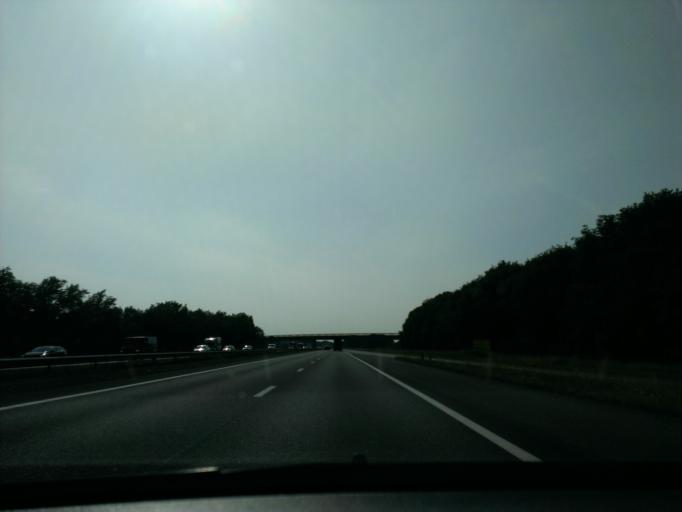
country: NL
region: Gelderland
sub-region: Gemeente Lochem
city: Laren
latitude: 52.2489
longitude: 6.3942
